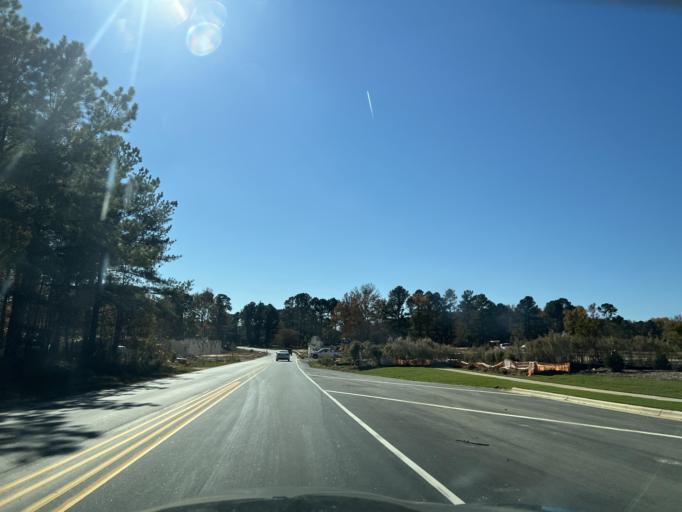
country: US
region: North Carolina
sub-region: Wake County
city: Garner
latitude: 35.6634
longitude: -78.7164
